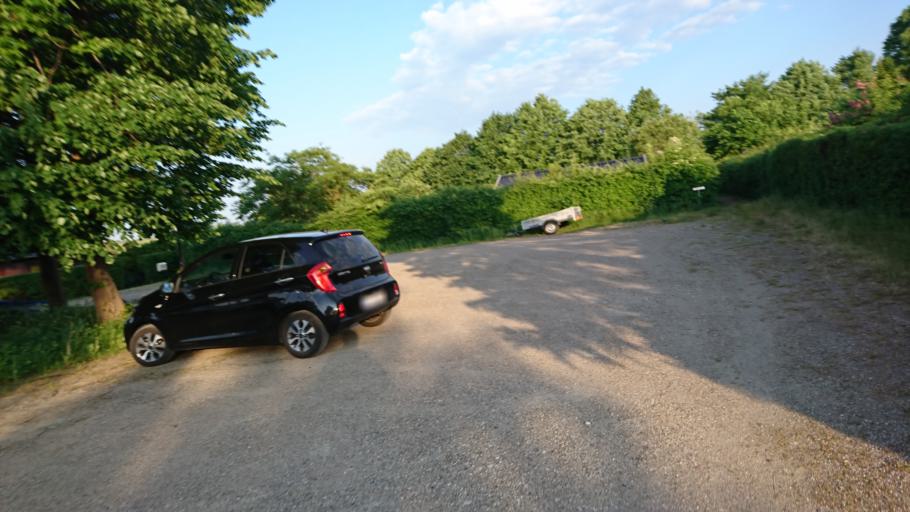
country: DK
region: Capital Region
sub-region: Egedal Kommune
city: Smorumnedre
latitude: 55.7172
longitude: 12.3286
